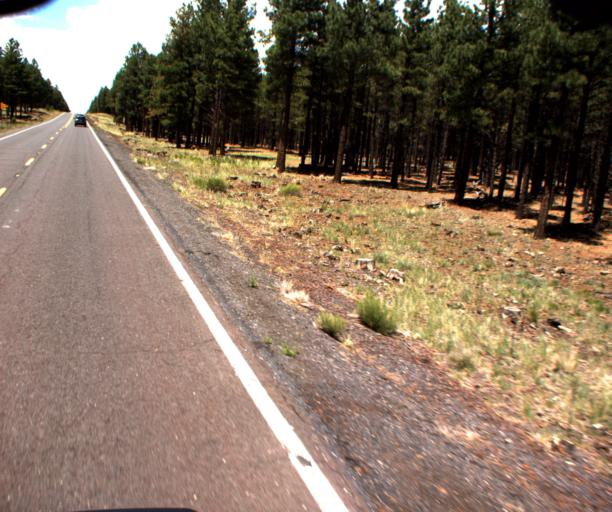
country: US
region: Arizona
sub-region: Coconino County
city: Parks
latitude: 35.4613
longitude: -111.7798
